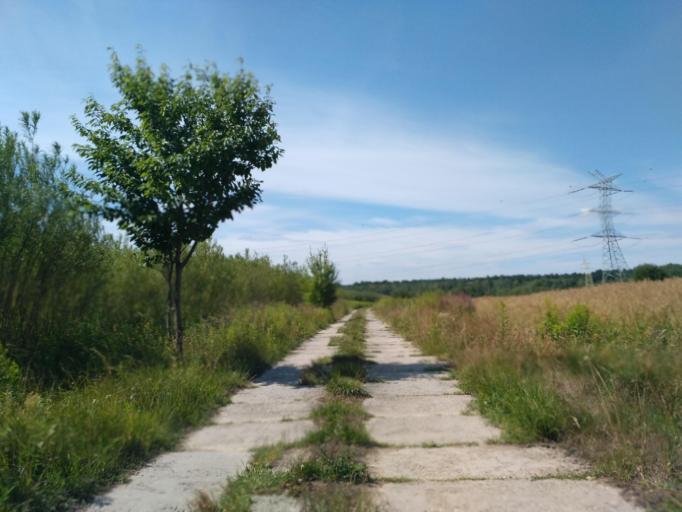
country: PL
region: Subcarpathian Voivodeship
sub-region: Powiat brzozowski
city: Haczow
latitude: 49.6507
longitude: 21.8591
